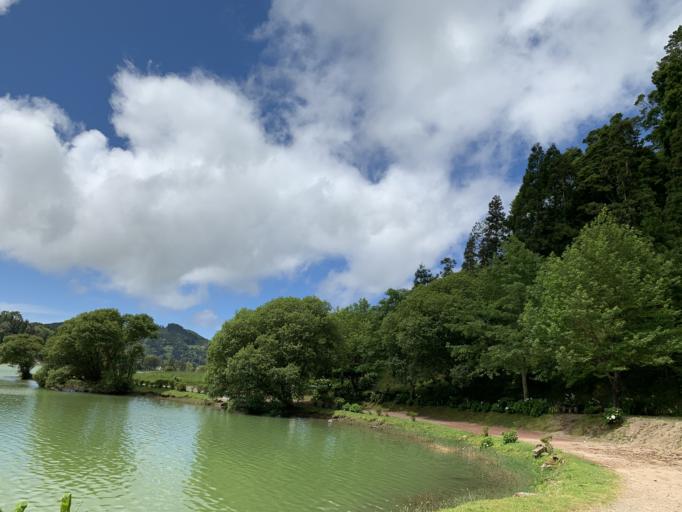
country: PT
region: Azores
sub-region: Ponta Delgada
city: Arrifes
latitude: 37.8485
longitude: -25.7849
